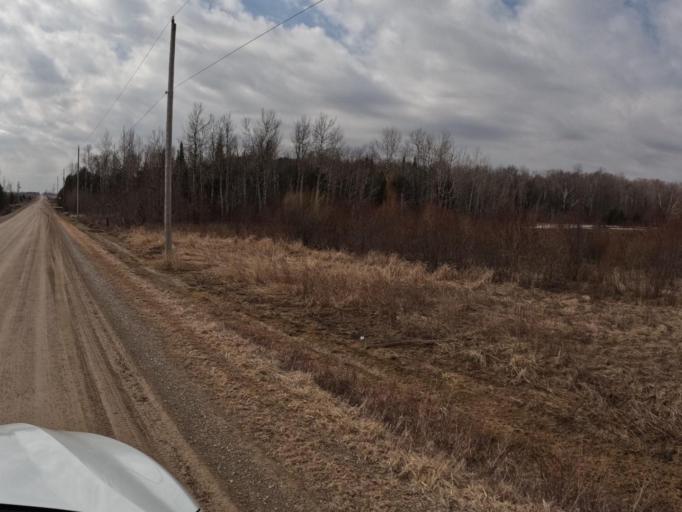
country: CA
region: Ontario
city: Orangeville
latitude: 43.9312
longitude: -80.2204
